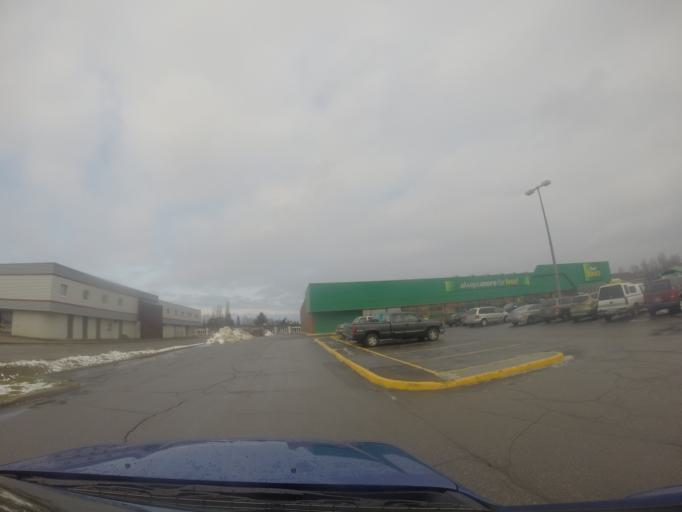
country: CA
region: Ontario
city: Greater Sudbury
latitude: 46.5224
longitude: -80.9308
